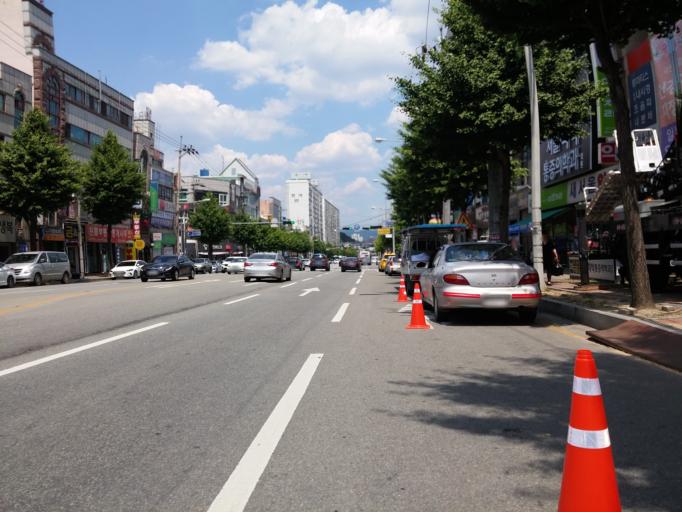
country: KR
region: Chungcheongbuk-do
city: Cheongju-si
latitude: 36.6267
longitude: 127.4348
